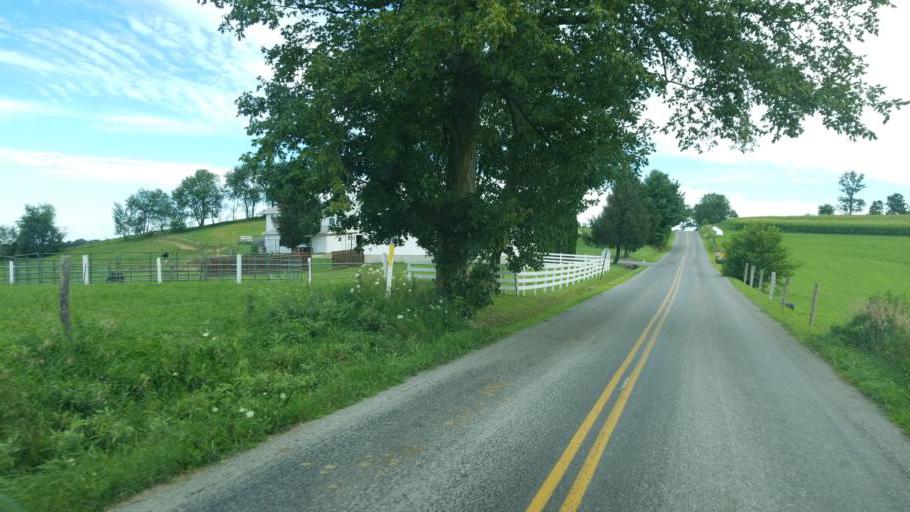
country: US
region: Ohio
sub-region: Holmes County
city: Millersburg
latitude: 40.4930
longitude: -81.7943
